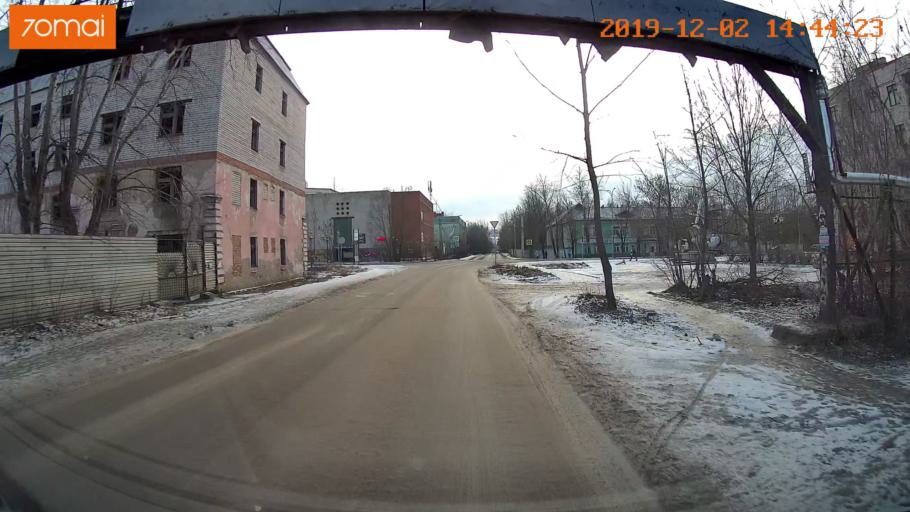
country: RU
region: Ivanovo
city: Bogorodskoye
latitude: 56.9898
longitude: 41.0376
